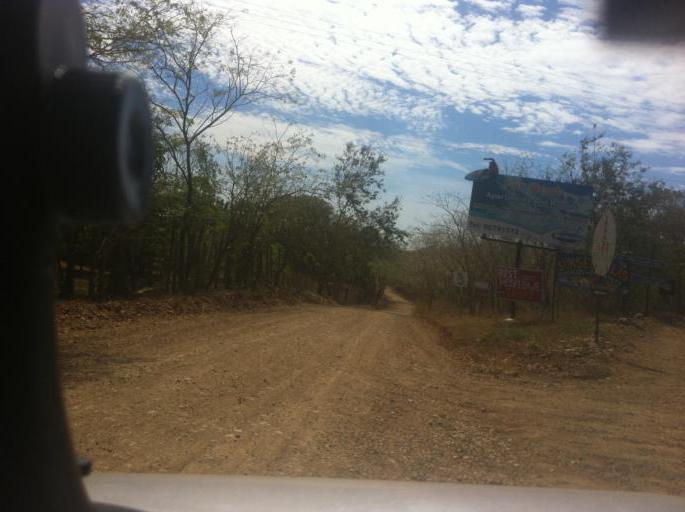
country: NI
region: Rivas
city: Tola
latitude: 11.4845
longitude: -86.0967
